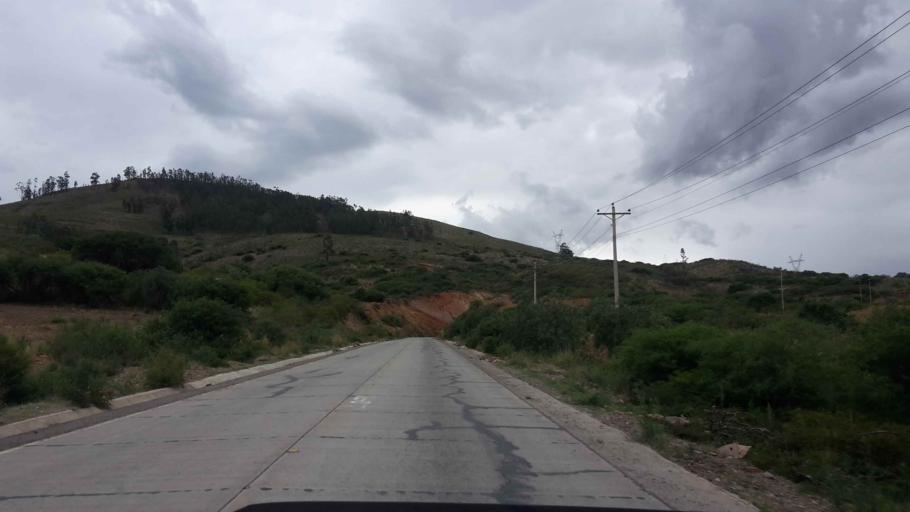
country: BO
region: Cochabamba
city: Cochabamba
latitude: -17.5331
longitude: -66.2021
